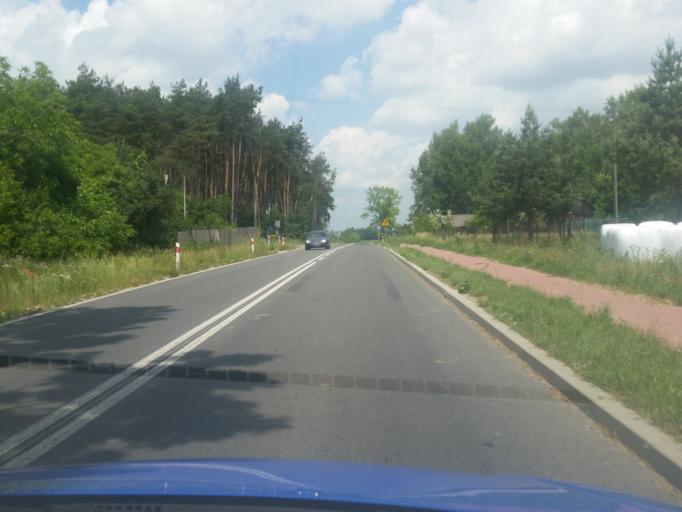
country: PL
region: Swietokrzyskie
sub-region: Powiat buski
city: Wislica
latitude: 50.3889
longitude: 20.6947
